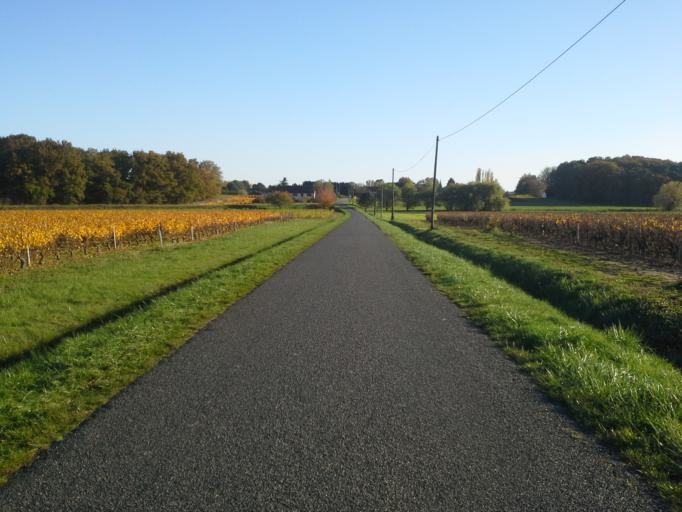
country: FR
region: Centre
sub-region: Departement du Loir-et-Cher
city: Saint-Romain-sur-Cher
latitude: 47.3690
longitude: 1.4004
